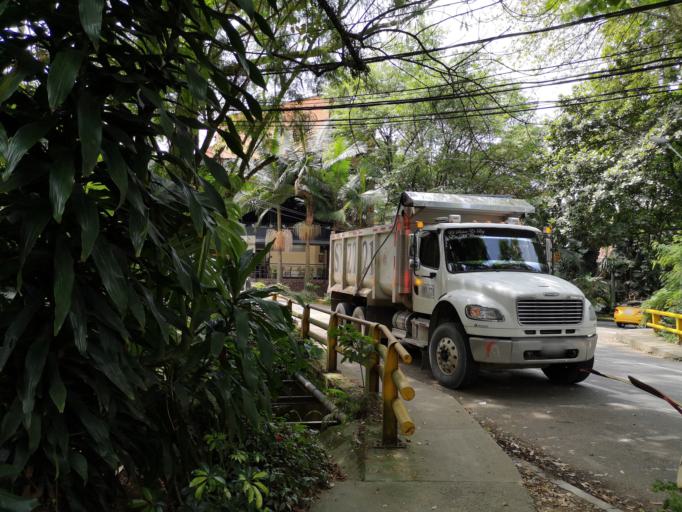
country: CO
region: Antioquia
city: Itagui
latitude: 6.2077
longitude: -75.5647
